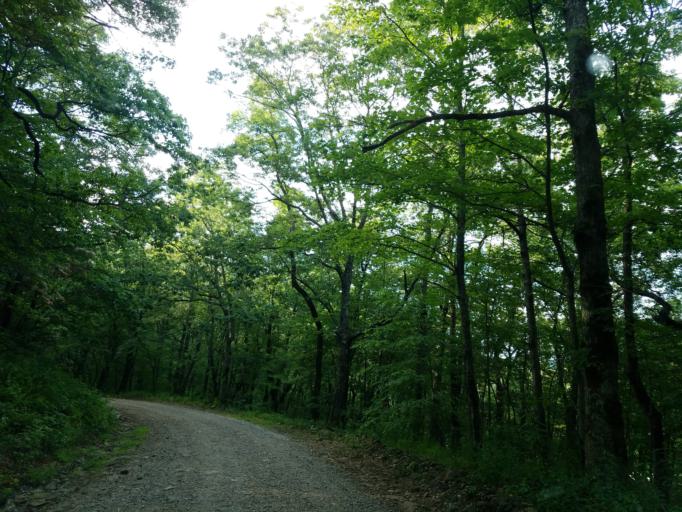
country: US
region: Georgia
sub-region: Lumpkin County
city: Dahlonega
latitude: 34.6540
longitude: -84.1334
